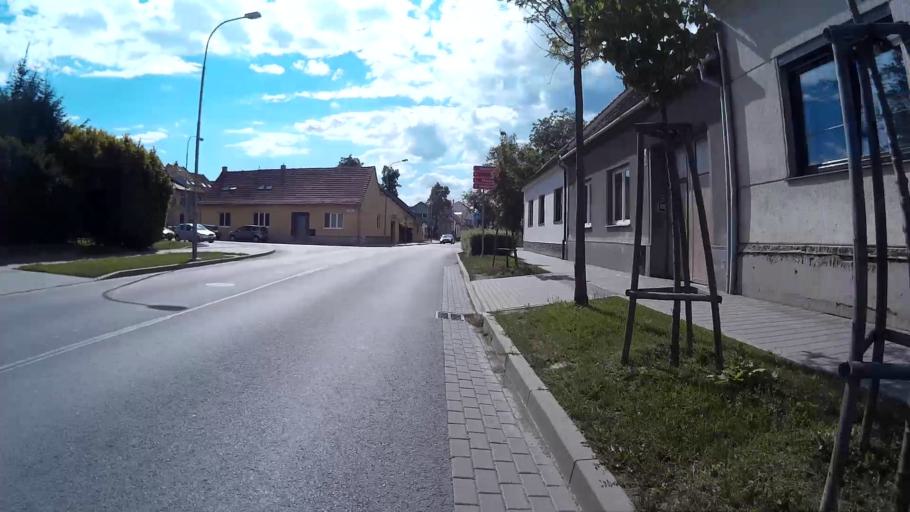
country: CZ
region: South Moravian
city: Ostopovice
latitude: 49.1647
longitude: 16.5626
